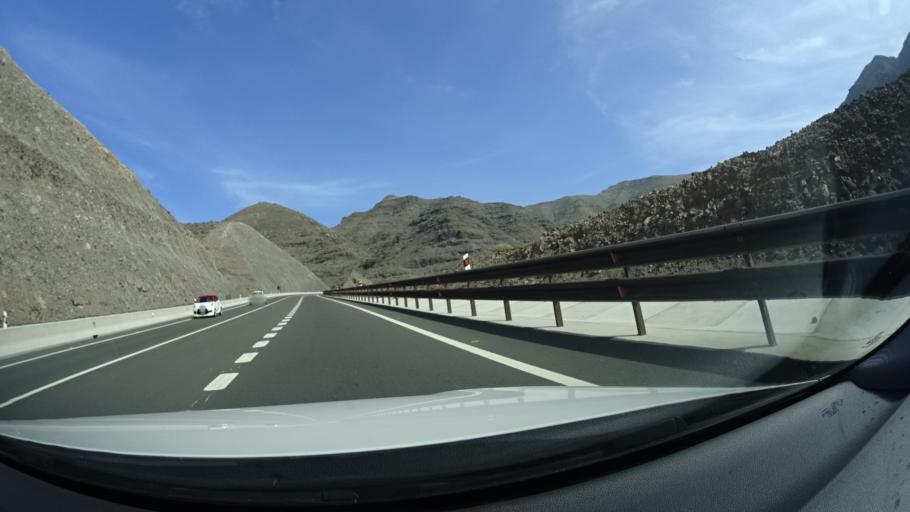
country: ES
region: Canary Islands
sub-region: Provincia de Las Palmas
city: San Nicolas
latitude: 28.0160
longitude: -15.7713
